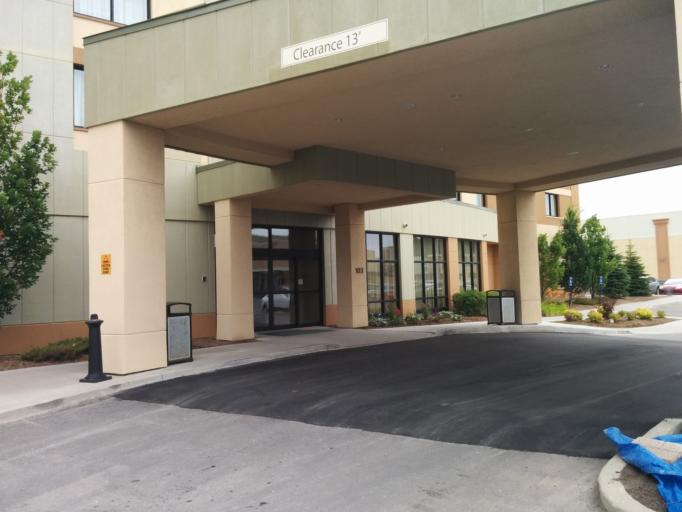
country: CA
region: Ontario
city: Kingston
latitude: 44.2667
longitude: -76.5035
